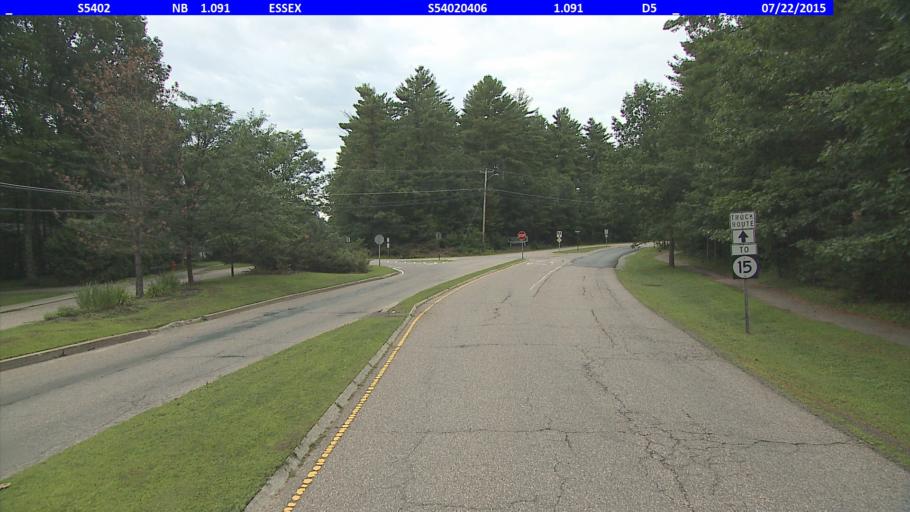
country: US
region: Vermont
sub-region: Chittenden County
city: Jericho
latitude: 44.4941
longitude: -73.0497
